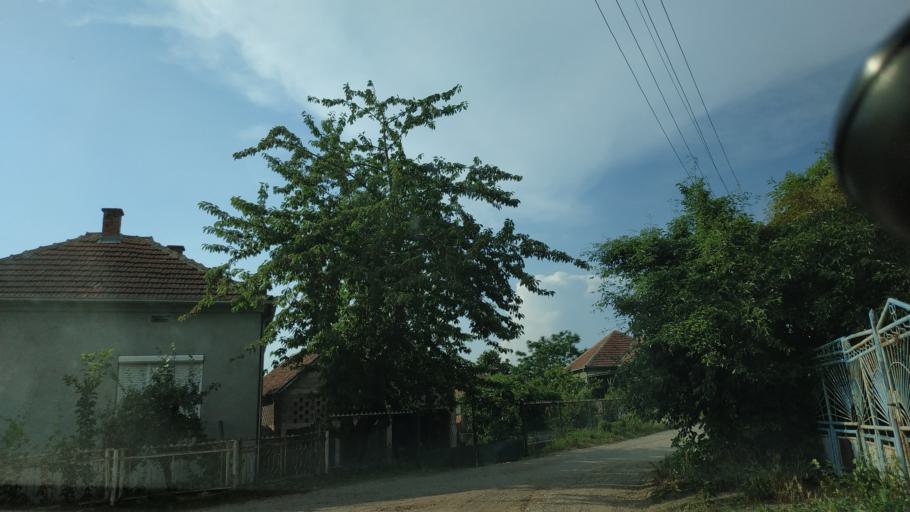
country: RS
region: Central Serbia
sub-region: Nisavski Okrug
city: Aleksinac
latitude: 43.6061
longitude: 21.6929
